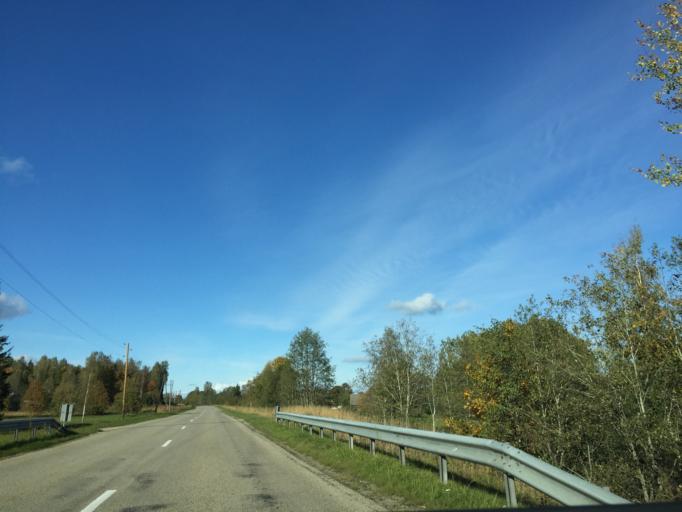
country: LV
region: Rojas
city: Roja
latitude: 57.4419
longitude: 22.9039
